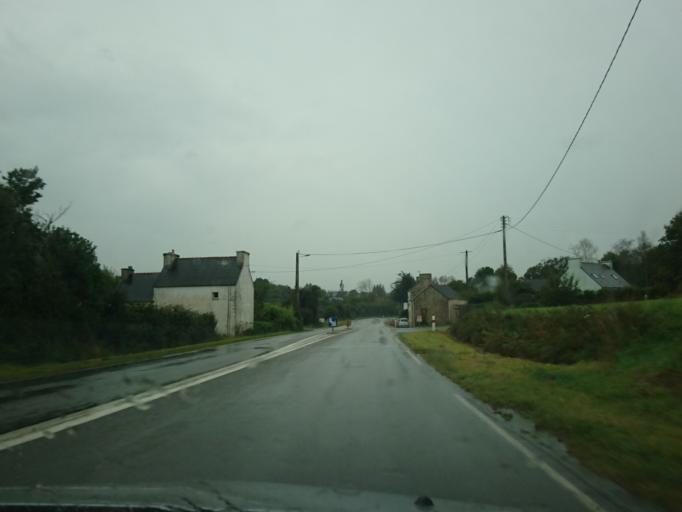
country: FR
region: Brittany
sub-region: Departement du Finistere
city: Le Drennec
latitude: 48.5402
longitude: -4.3651
